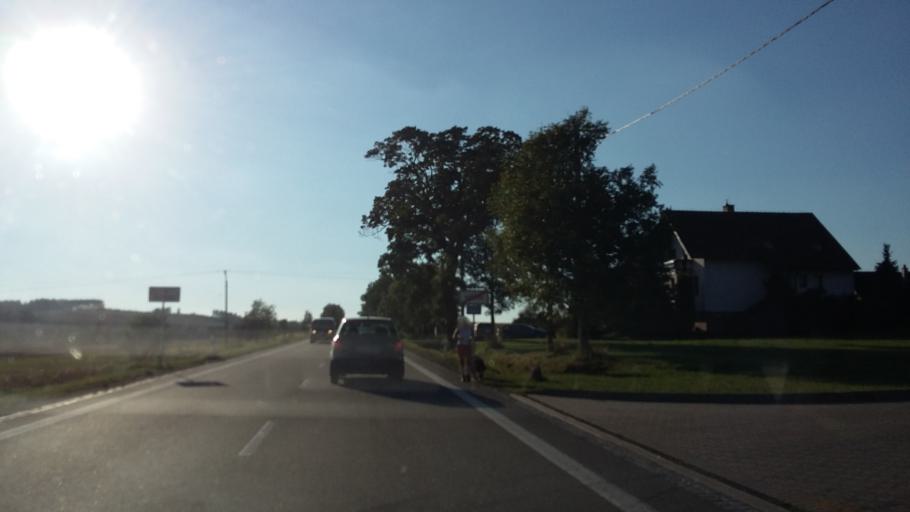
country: CZ
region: Vysocina
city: Merin
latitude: 49.3959
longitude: 15.8765
